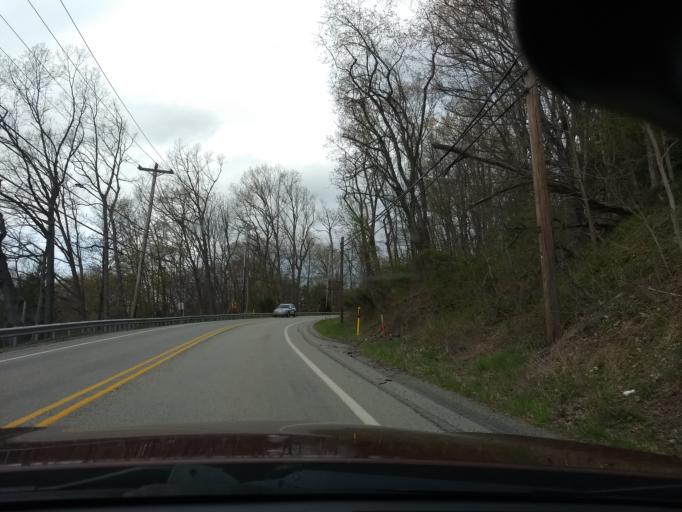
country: US
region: Pennsylvania
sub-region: Allegheny County
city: Fox Chapel
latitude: 40.5502
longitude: -79.8851
